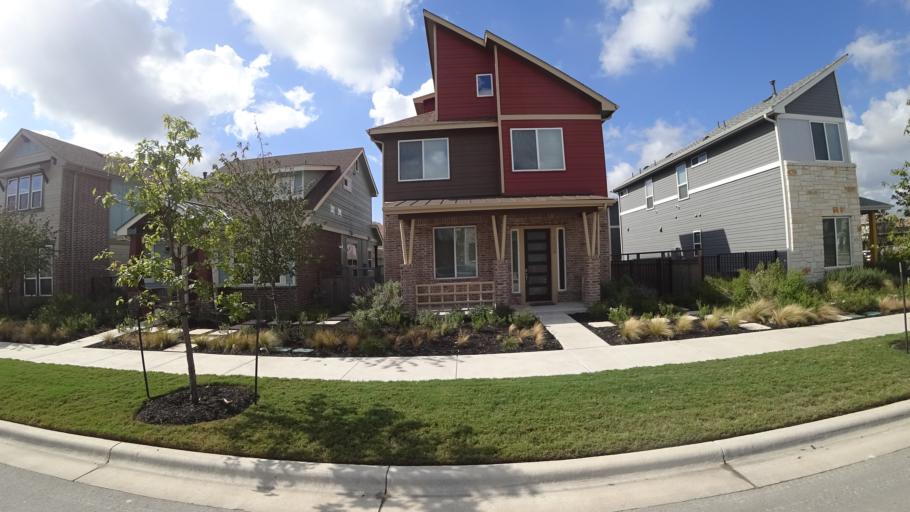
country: US
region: Texas
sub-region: Travis County
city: Austin
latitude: 30.3436
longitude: -97.7186
